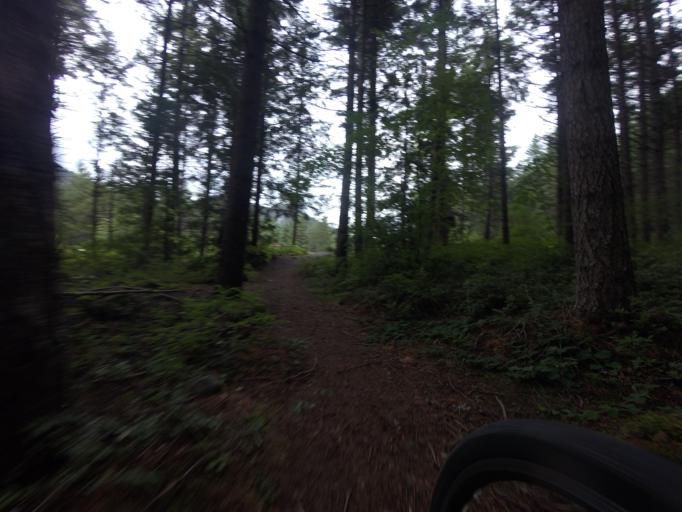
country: CA
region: British Columbia
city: Pemberton
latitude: 50.2199
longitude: -122.8819
